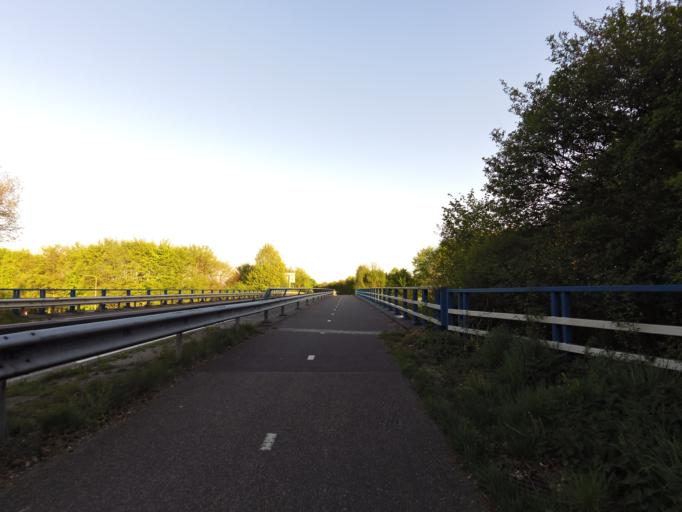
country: NL
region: Gelderland
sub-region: Oude IJsselstreek
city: Varsseveld
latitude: 51.9469
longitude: 6.4381
